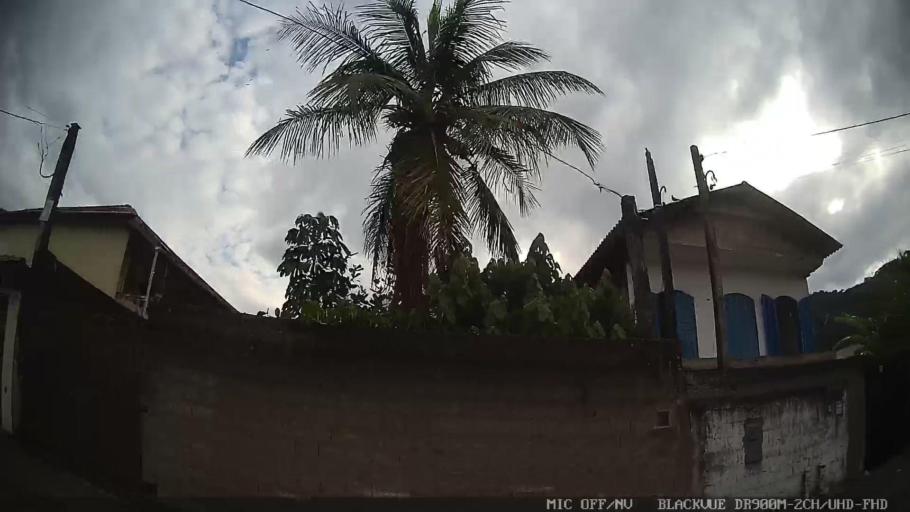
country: BR
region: Sao Paulo
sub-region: Guaruja
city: Guaruja
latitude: -23.9793
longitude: -46.2343
